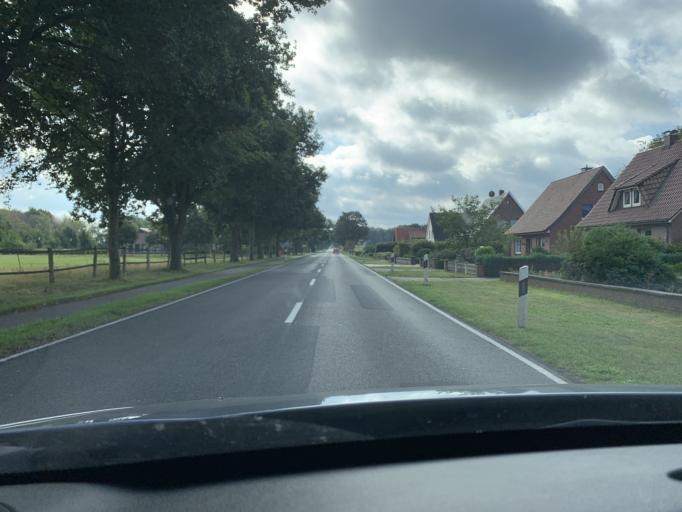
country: DE
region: Lower Saxony
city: Wardenburg
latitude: 53.0840
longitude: 8.1205
